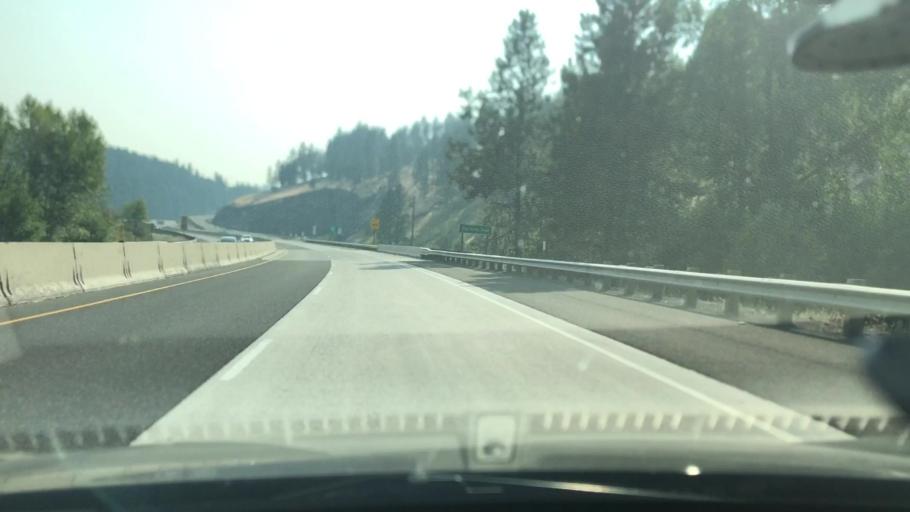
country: US
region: Oregon
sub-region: Union County
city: La Grande
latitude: 45.3473
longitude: -118.2219
